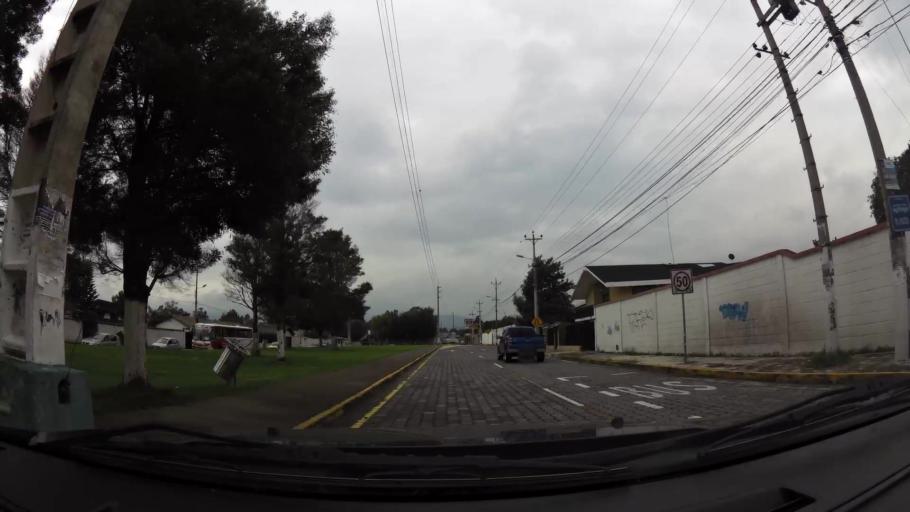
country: EC
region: Pichincha
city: Sangolqui
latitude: -0.3117
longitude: -78.4569
